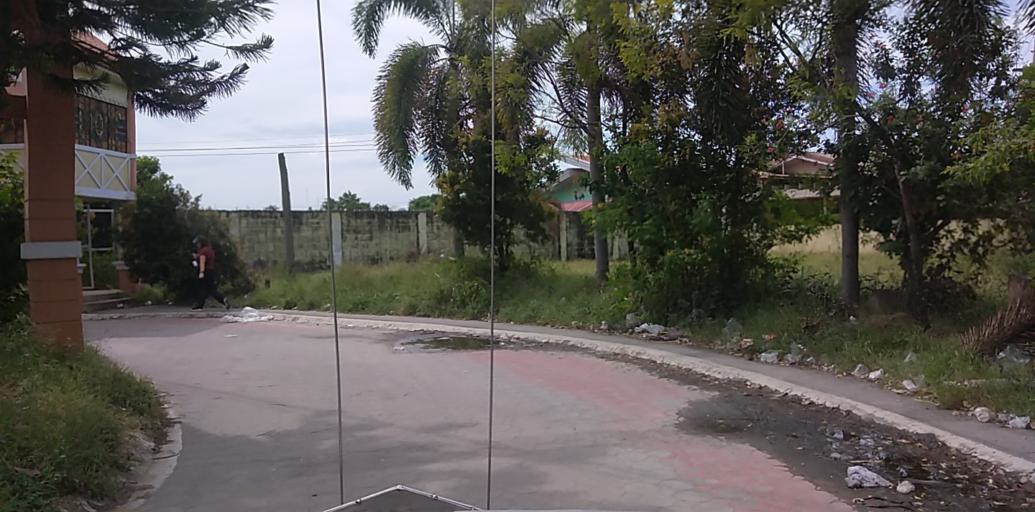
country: PH
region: Central Luzon
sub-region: Province of Pampanga
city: Manibaug Pasig
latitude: 15.1125
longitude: 120.5619
